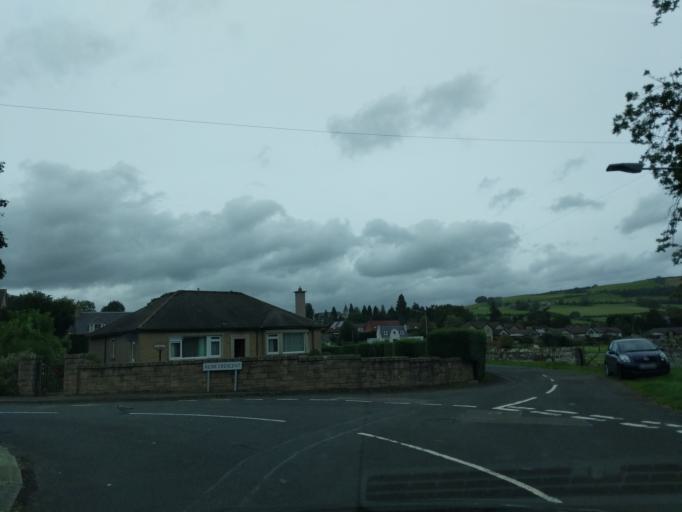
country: GB
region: Scotland
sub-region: The Scottish Borders
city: Melrose
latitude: 55.5993
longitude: -2.7410
